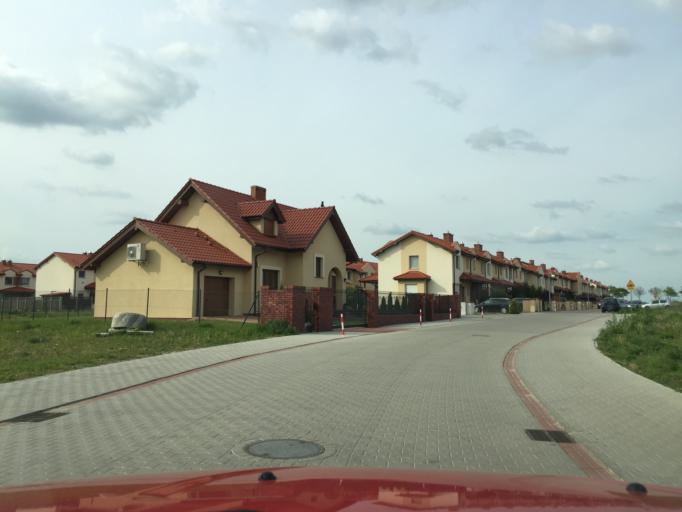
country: PL
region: Greater Poland Voivodeship
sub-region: Powiat poznanski
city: Plewiska
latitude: 52.3898
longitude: 16.7721
